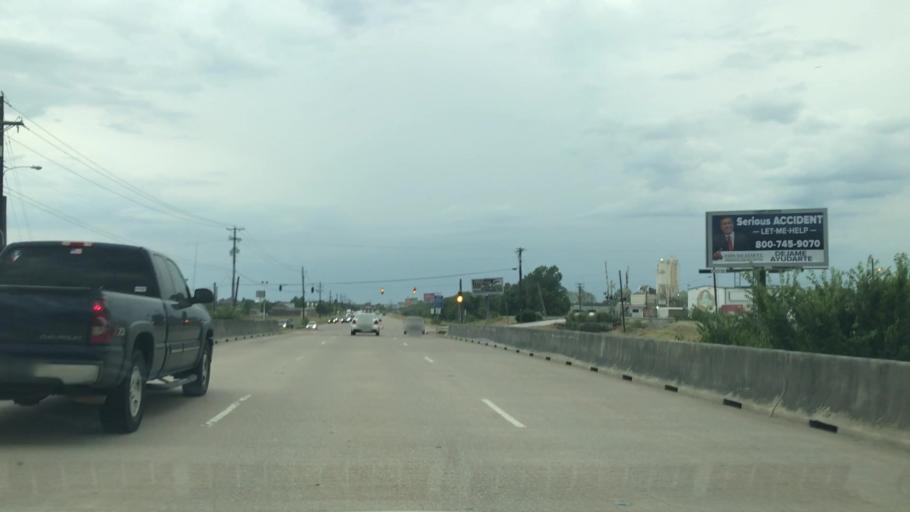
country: US
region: Texas
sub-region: Dallas County
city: Carrollton
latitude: 32.9515
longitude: -96.9389
